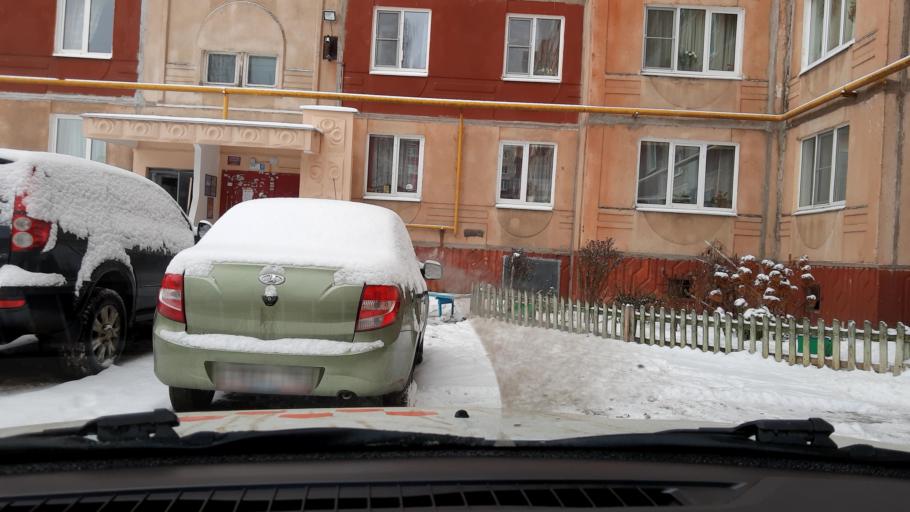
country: RU
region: Nizjnij Novgorod
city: Pyra
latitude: 56.2277
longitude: 43.3779
